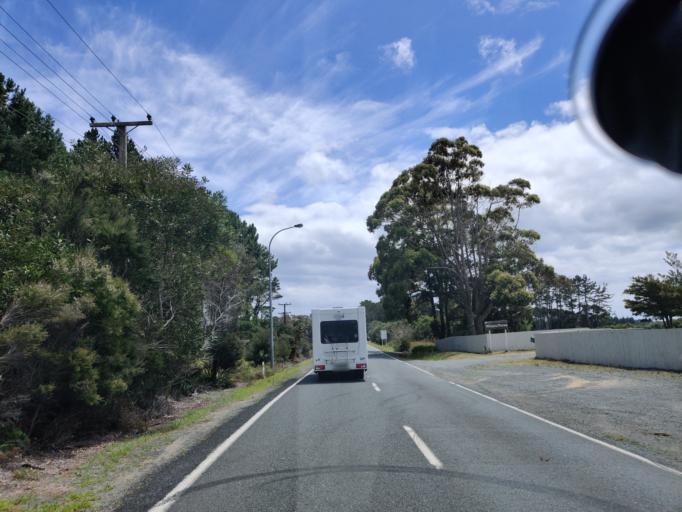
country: NZ
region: Northland
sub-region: Far North District
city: Kaitaia
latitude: -34.7430
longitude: 173.0468
